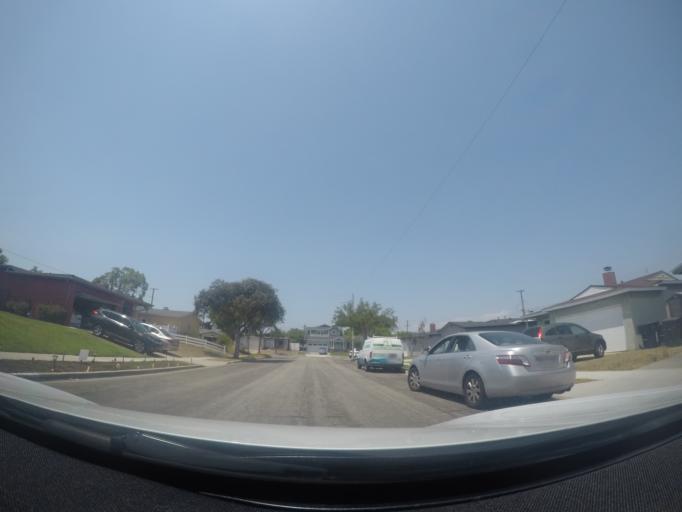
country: US
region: California
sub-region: Los Angeles County
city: Torrance
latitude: 33.8199
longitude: -118.3607
